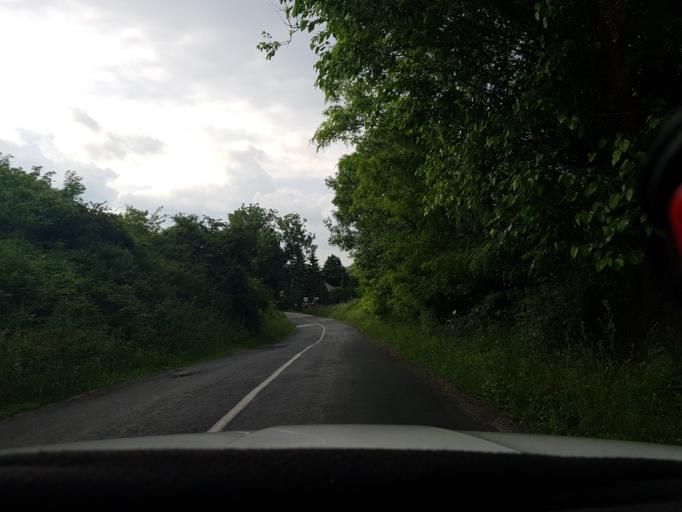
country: HU
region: Komarom-Esztergom
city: Nyergesujfalu
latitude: 47.7179
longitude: 18.5629
